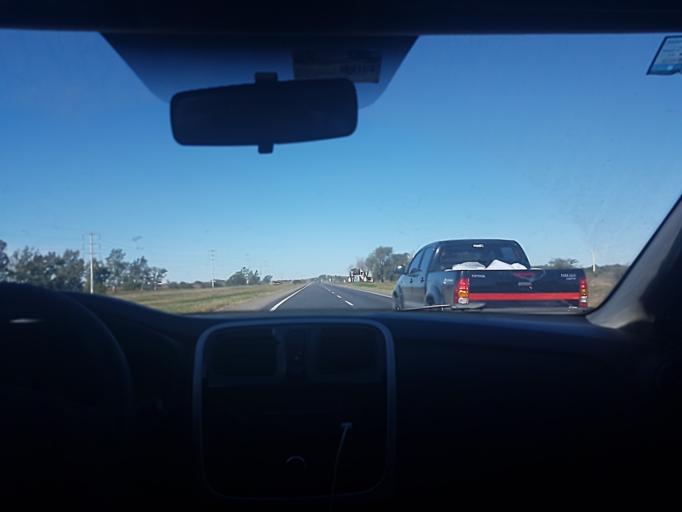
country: AR
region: Cordoba
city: Pilar
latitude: -31.6462
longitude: -63.8610
